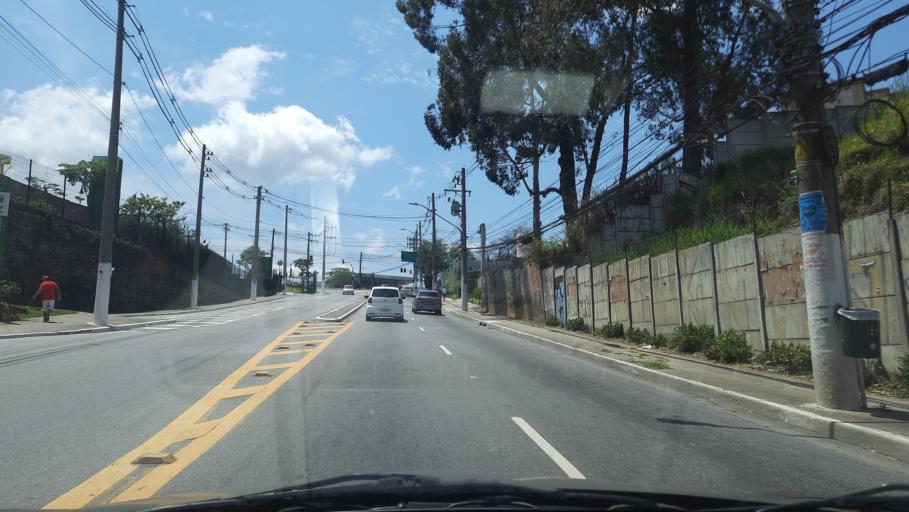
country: BR
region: Sao Paulo
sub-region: Caieiras
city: Caieiras
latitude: -23.4472
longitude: -46.7238
